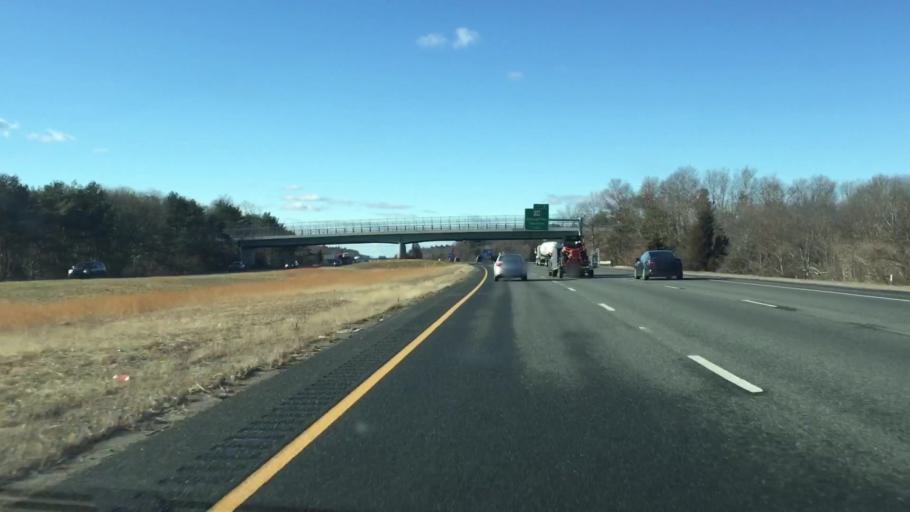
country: US
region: Massachusetts
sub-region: Bristol County
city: Raynham
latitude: 41.9573
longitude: -71.0417
